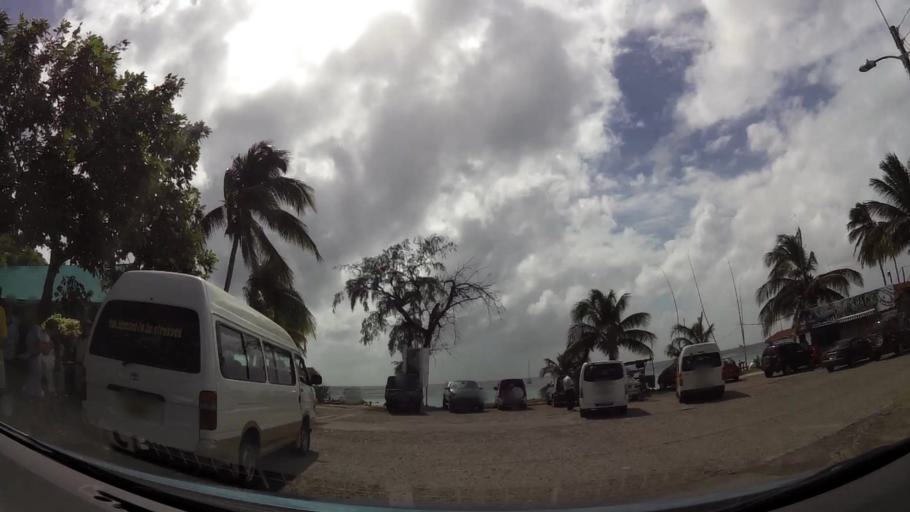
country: KN
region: Saint George Basseterre
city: Basseterre
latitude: 17.2807
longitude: -62.6867
